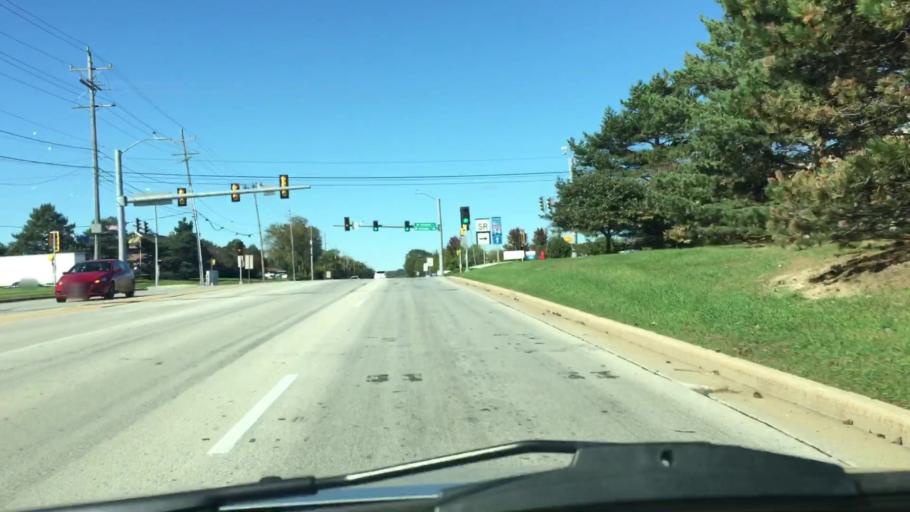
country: US
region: Wisconsin
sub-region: Waukesha County
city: Waukesha
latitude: 43.0364
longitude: -88.1850
